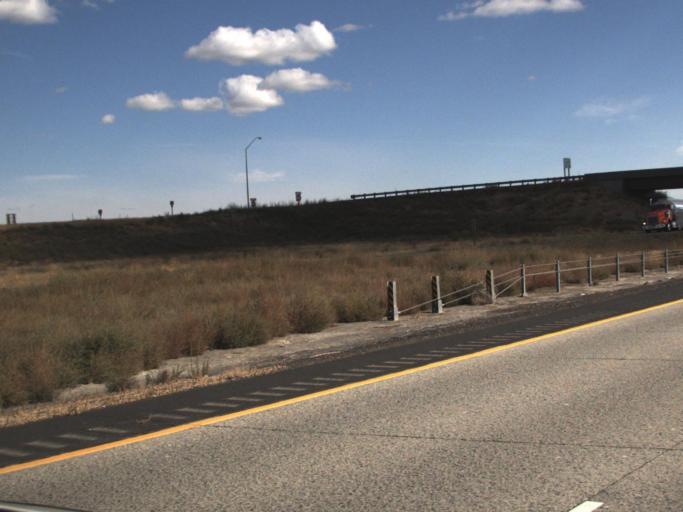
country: US
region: Washington
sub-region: Yakima County
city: Grandview
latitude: 46.2562
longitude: -119.8797
